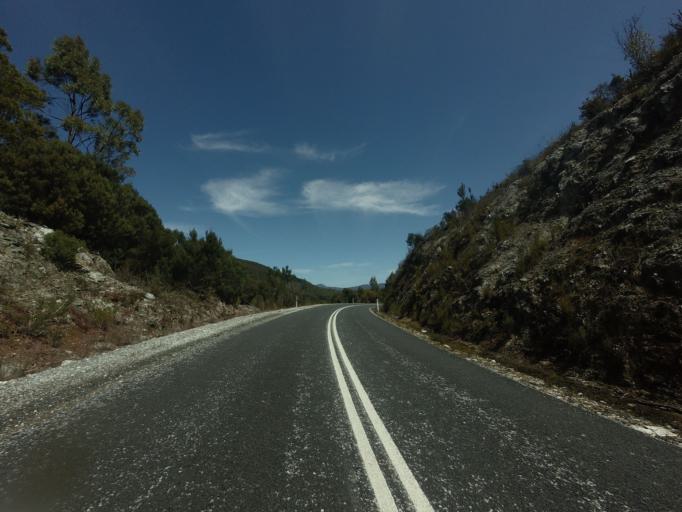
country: AU
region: Tasmania
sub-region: West Coast
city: Queenstown
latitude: -42.7957
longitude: 146.0827
